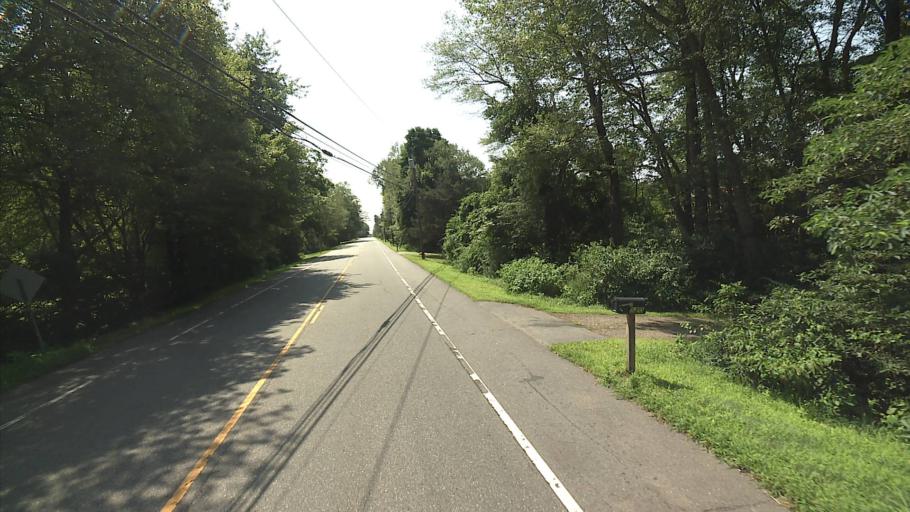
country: US
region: Connecticut
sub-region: New London County
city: Colchester
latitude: 41.5502
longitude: -72.2783
